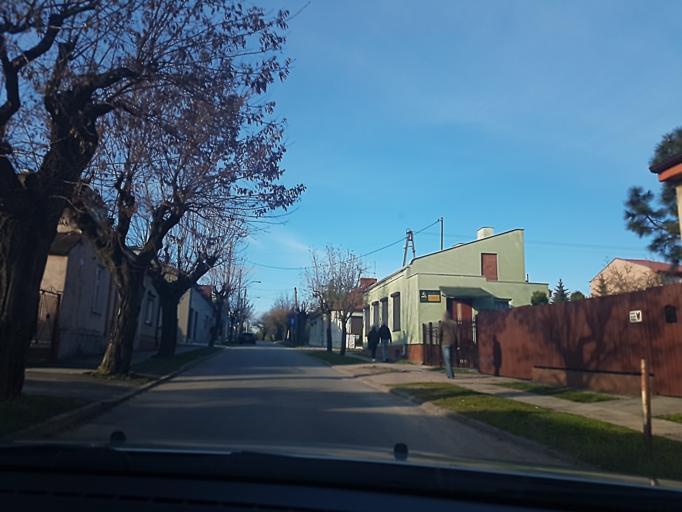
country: PL
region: Lodz Voivodeship
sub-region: Powiat kutnowski
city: Kutno
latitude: 52.2367
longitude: 19.3577
